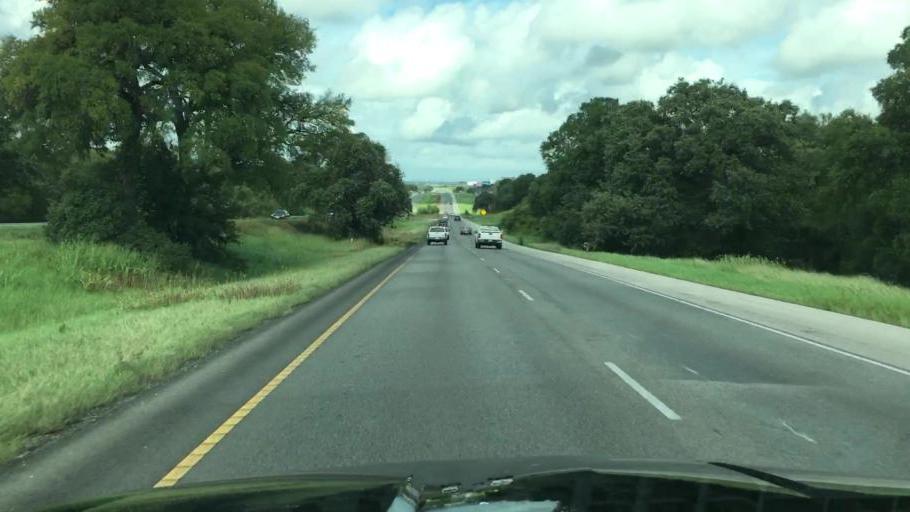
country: US
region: Texas
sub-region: Bastrop County
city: Wyldwood
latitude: 30.1539
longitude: -97.4923
